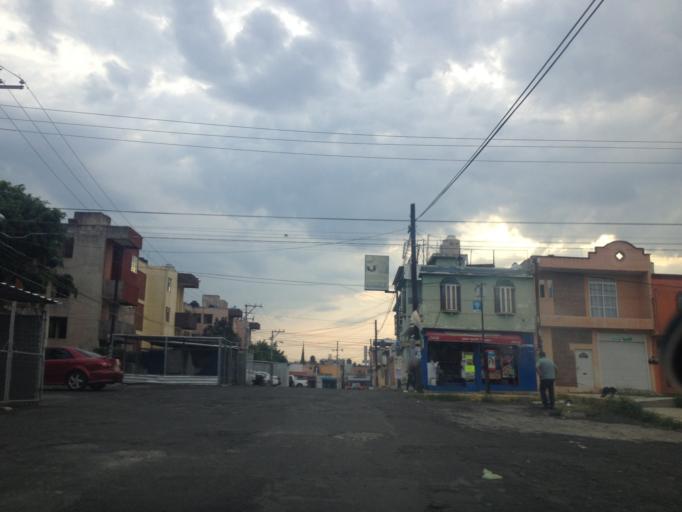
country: MX
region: Michoacan
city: Morelia
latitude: 19.7058
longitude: -101.2343
